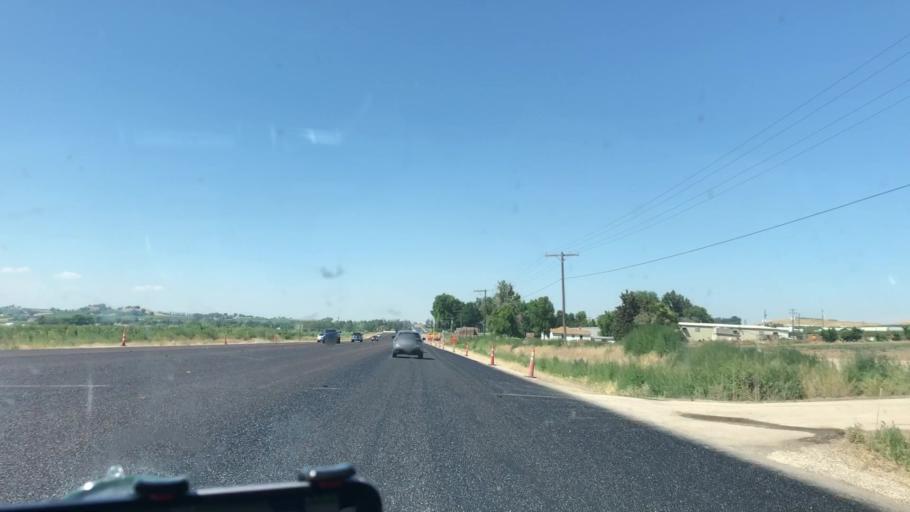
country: US
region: Idaho
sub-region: Owyhee County
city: Marsing
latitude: 43.5708
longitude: -116.7924
